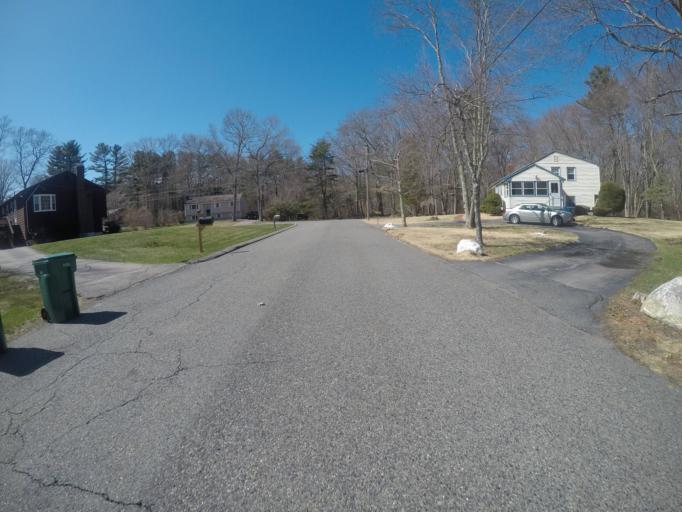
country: US
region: Massachusetts
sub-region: Bristol County
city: Easton
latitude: 42.0102
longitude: -71.1033
